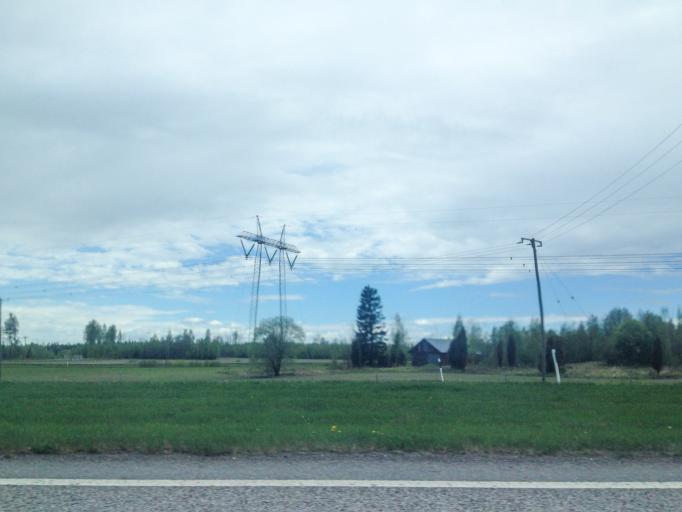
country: FI
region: Uusimaa
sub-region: Helsinki
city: Nurmijaervi
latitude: 60.5398
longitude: 24.8399
